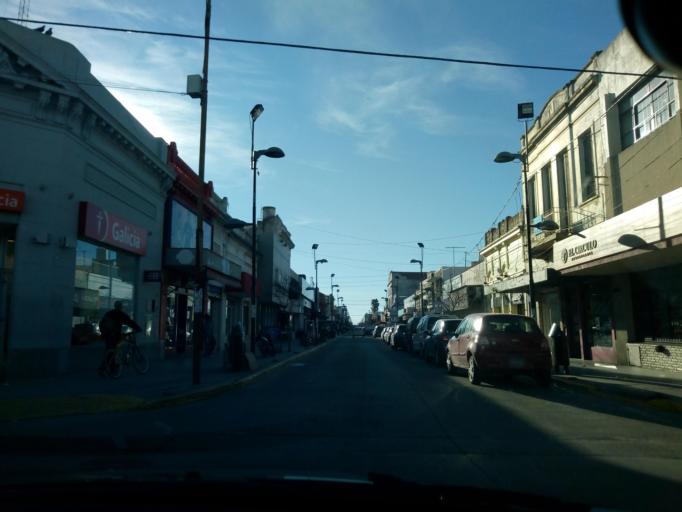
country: AR
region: Buenos Aires
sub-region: Partido de Ensenada
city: Ensenada
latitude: -34.8614
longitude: -57.9022
